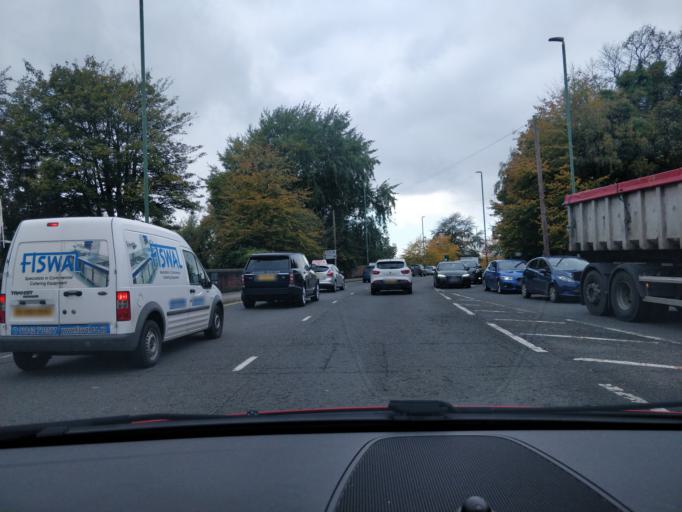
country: GB
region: England
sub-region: Lancashire
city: Ormskirk
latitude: 53.5657
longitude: -2.8835
